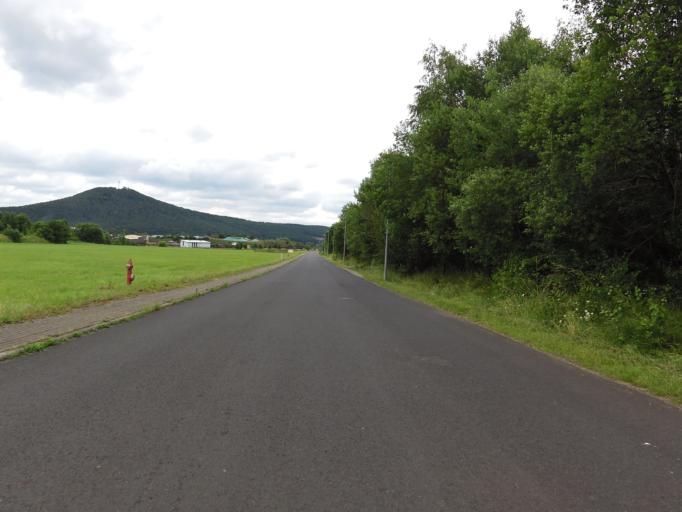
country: DE
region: Thuringia
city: Stadtlengsfeld
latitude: 50.8169
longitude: 10.1339
